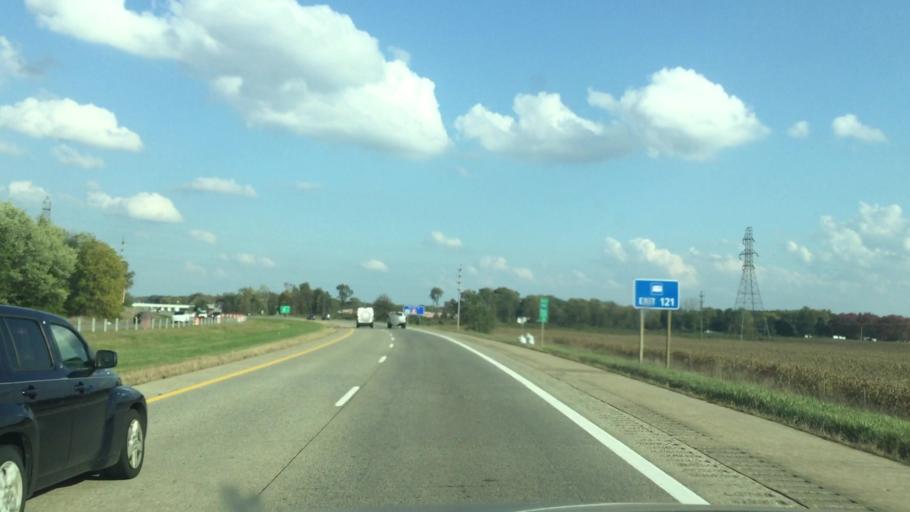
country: US
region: Michigan
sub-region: Calhoun County
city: Albion
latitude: 42.2640
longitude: -84.7694
